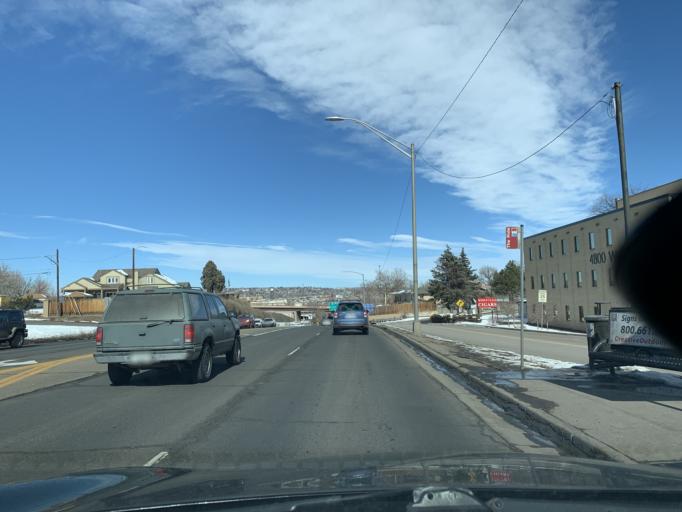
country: US
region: Colorado
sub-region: Jefferson County
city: Wheat Ridge
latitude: 39.7819
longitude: -105.0813
